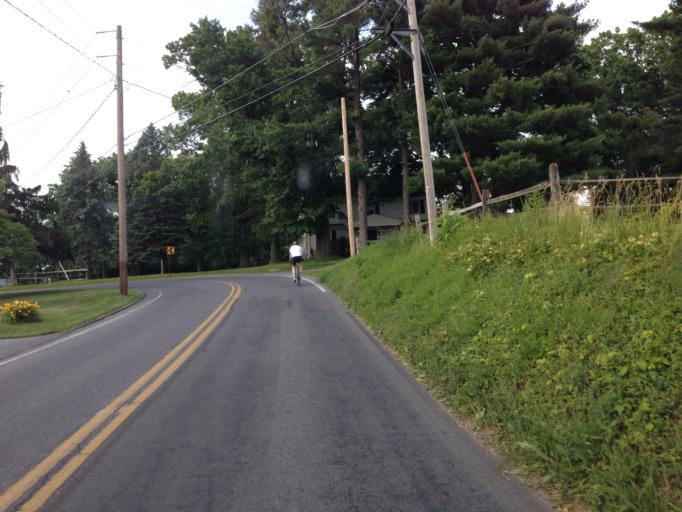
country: US
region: Pennsylvania
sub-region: Lancaster County
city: Rothsville
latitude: 40.1373
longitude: -76.2661
